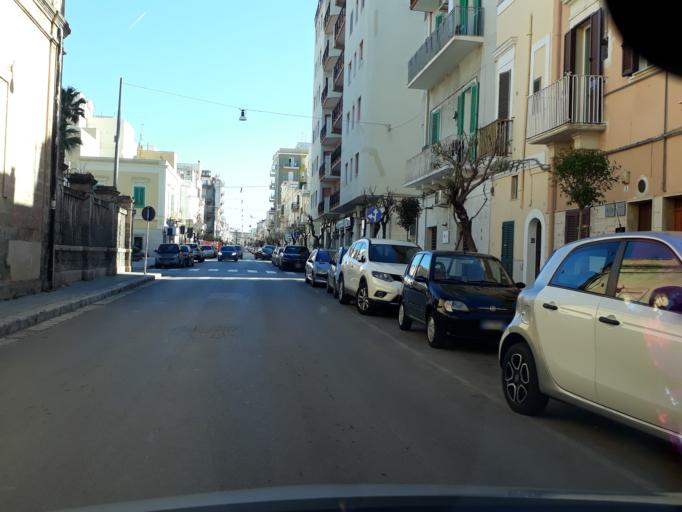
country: IT
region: Apulia
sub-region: Provincia di Bari
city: Monopoli
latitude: 40.9539
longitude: 17.2979
